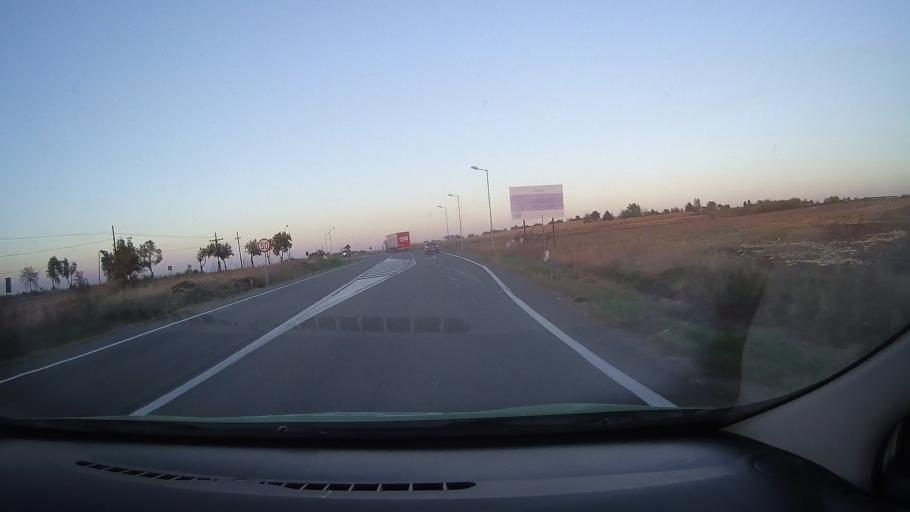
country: RO
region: Bihor
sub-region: Comuna Cherechiu
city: Cherechiu
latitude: 47.3752
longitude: 22.1363
